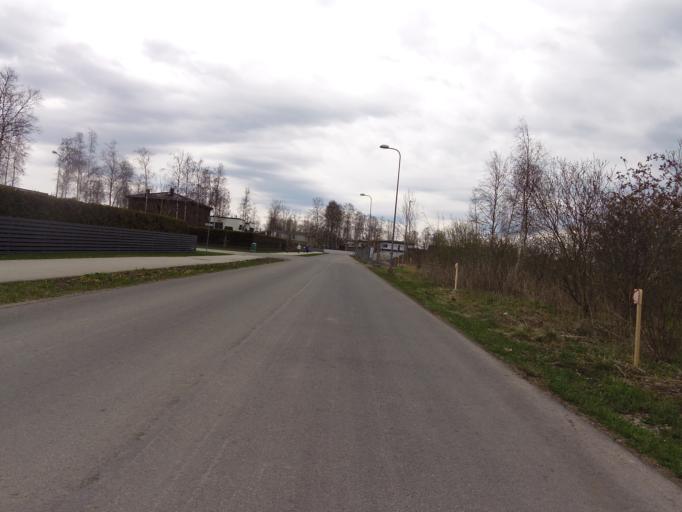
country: EE
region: Harju
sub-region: Tallinna linn
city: Tallinn
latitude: 59.4018
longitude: 24.7982
